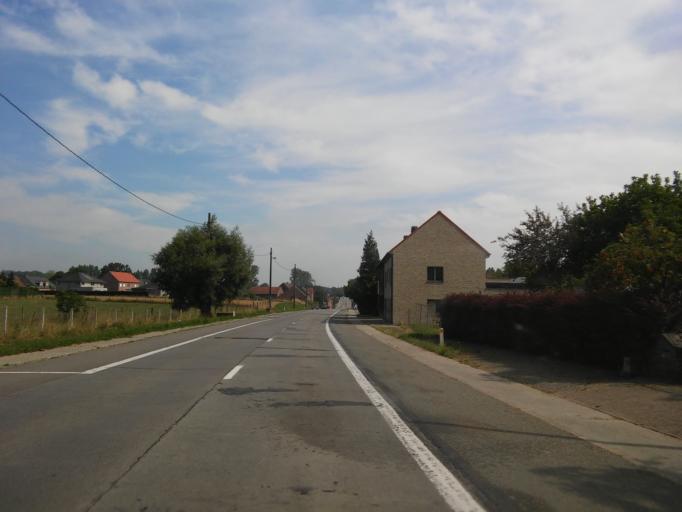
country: BE
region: Flanders
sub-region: Provincie Vlaams-Brabant
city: Gooik
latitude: 50.7573
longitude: 4.1067
